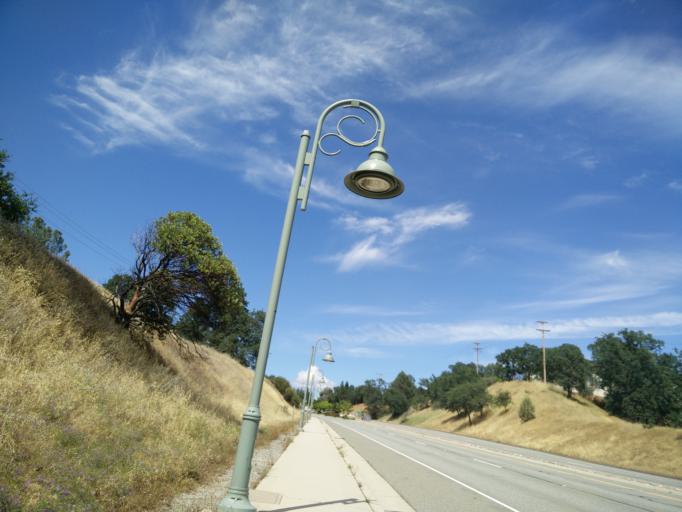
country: US
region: California
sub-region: Shasta County
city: Redding
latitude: 40.6045
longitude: -122.3792
